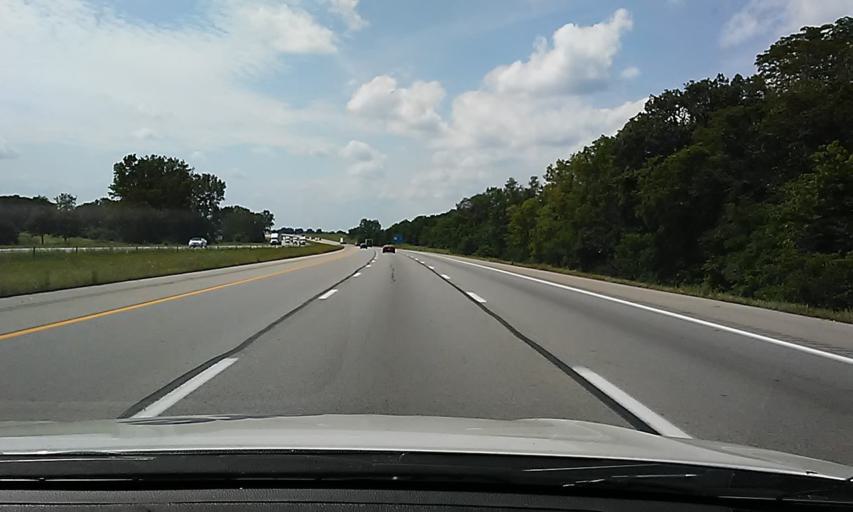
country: US
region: Ohio
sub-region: Clark County
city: Lisbon
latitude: 39.9359
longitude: -83.6570
